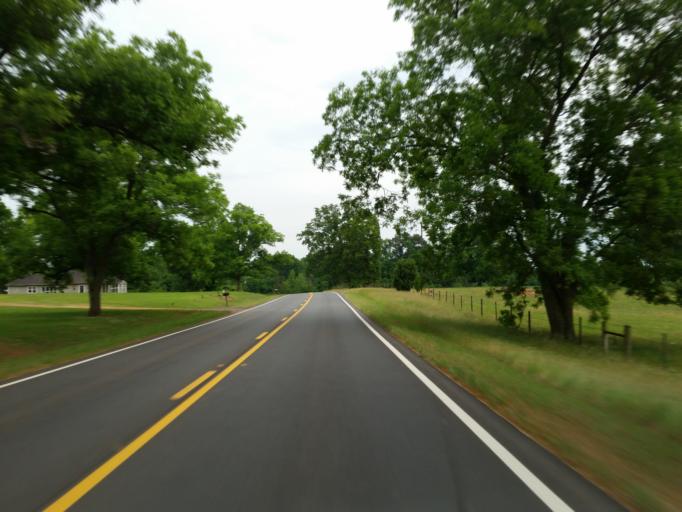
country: US
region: Georgia
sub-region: Dooly County
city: Unadilla
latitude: 32.3360
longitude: -83.7890
